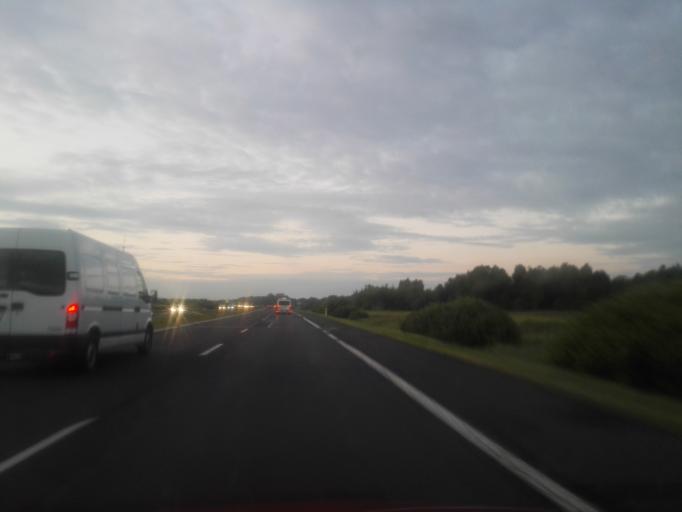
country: PL
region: Lodz Voivodeship
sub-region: Powiat radomszczanski
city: Kamiensk
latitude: 51.2292
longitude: 19.5101
